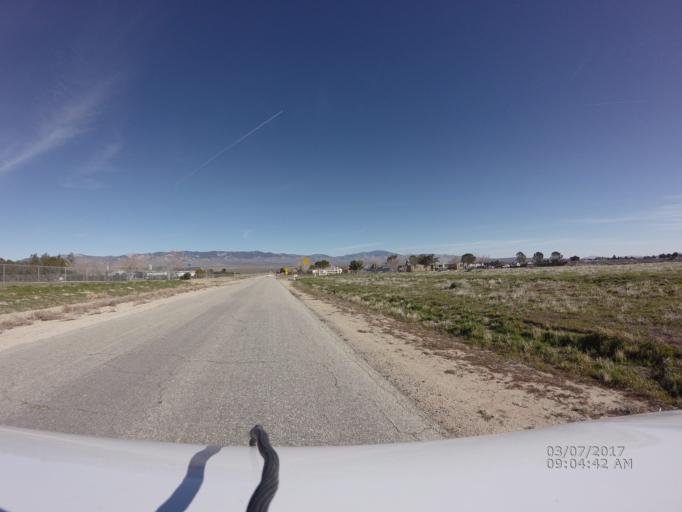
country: US
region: California
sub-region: Los Angeles County
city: Green Valley
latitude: 34.7940
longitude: -118.5812
